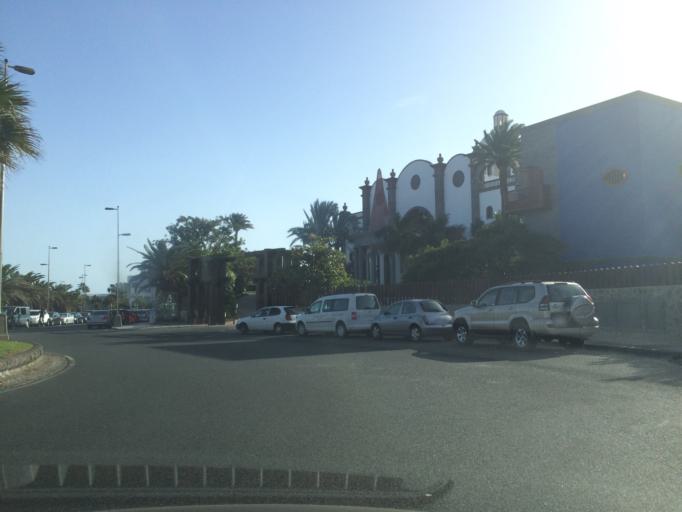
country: ES
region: Canary Islands
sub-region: Provincia de Las Palmas
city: Maspalomas
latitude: 27.7436
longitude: -15.6056
